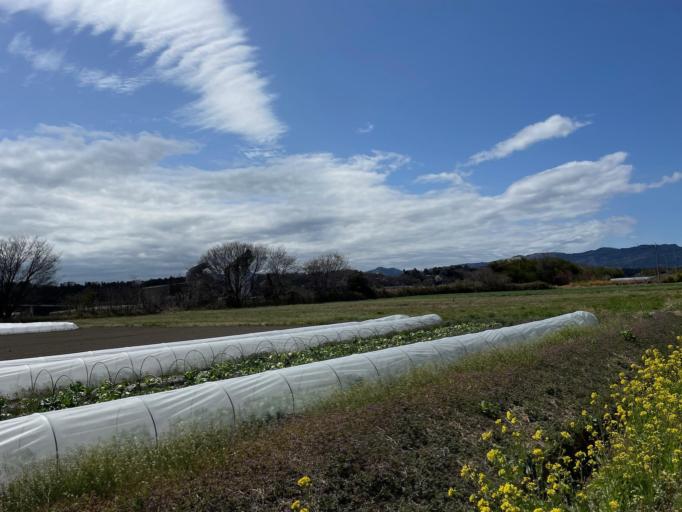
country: JP
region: Saitama
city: Yorii
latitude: 36.1210
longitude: 139.2460
